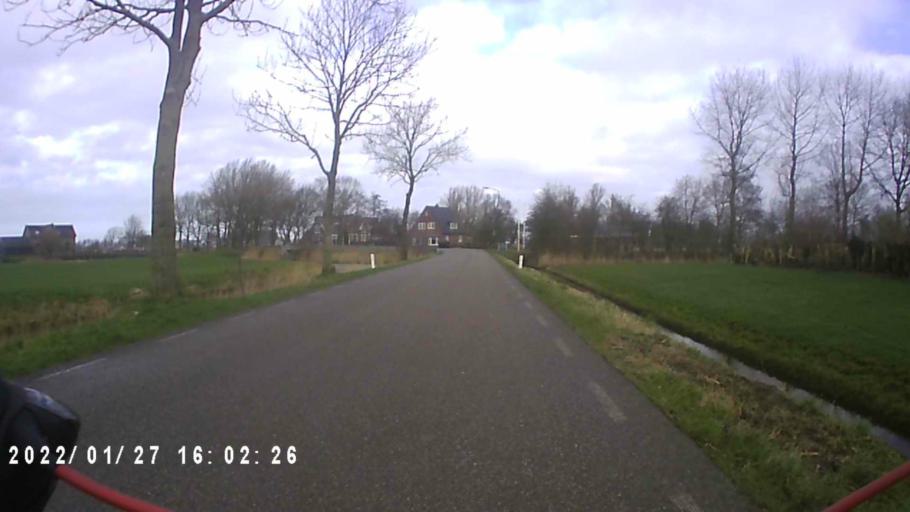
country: NL
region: Friesland
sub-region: Gemeente Dongeradeel
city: Anjum
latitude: 53.3751
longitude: 6.0892
